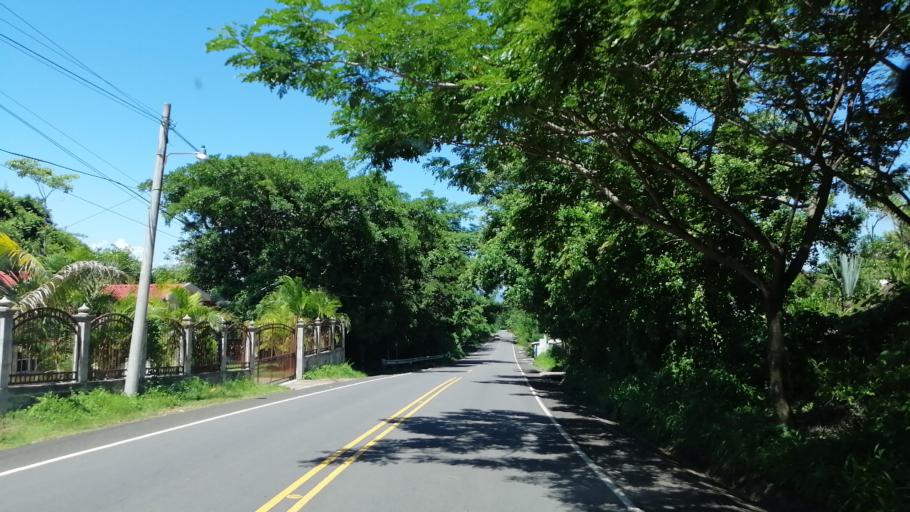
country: SV
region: Morazan
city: Cacaopera
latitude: 13.8114
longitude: -88.1679
